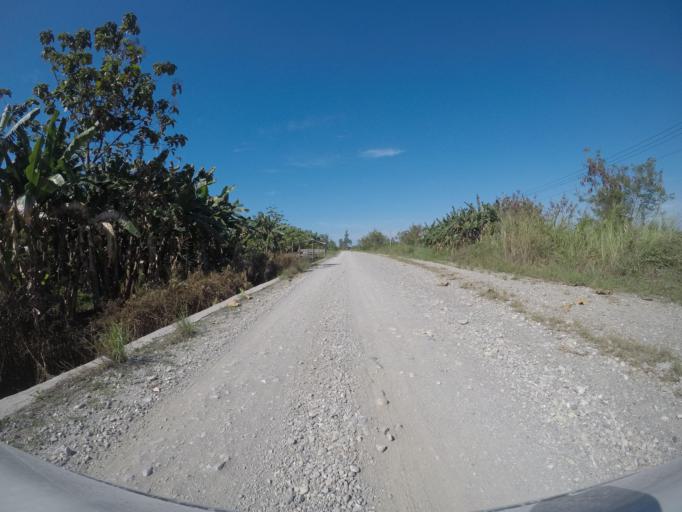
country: TL
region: Viqueque
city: Viqueque
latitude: -8.9437
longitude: 126.1128
